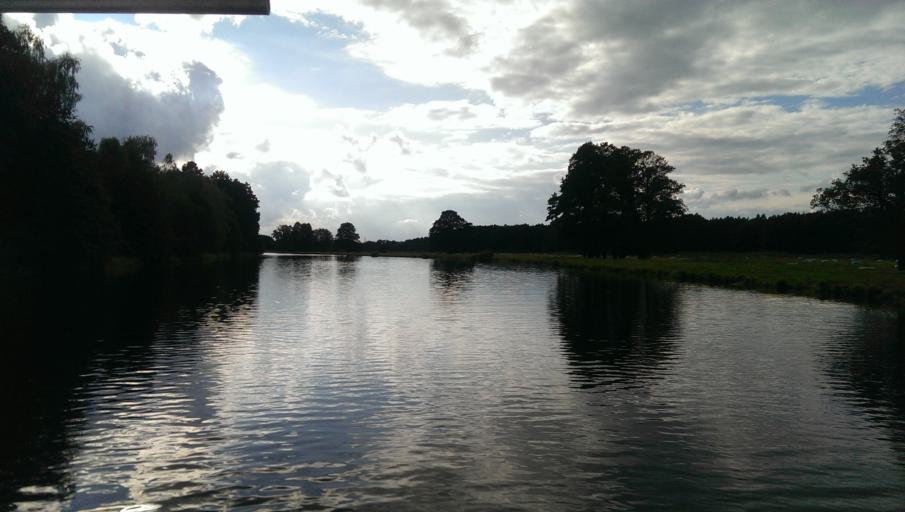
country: DE
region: Brandenburg
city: Liebenwalde
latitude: 52.8219
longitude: 13.3395
